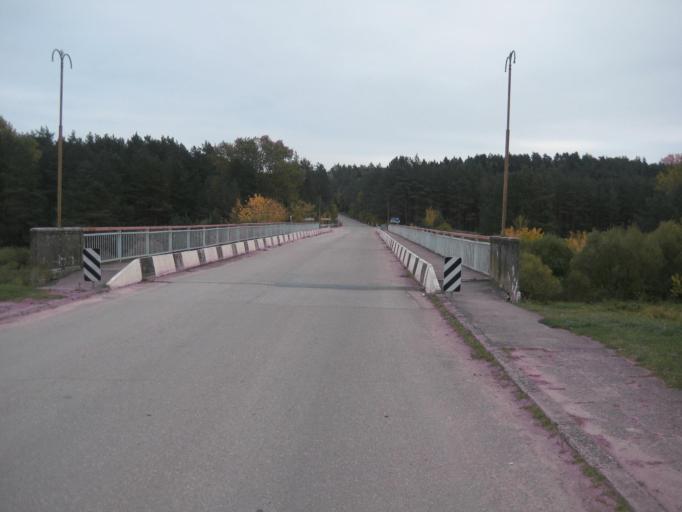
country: LT
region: Utenos apskritis
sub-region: Anyksciai
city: Anyksciai
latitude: 55.4347
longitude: 24.9361
